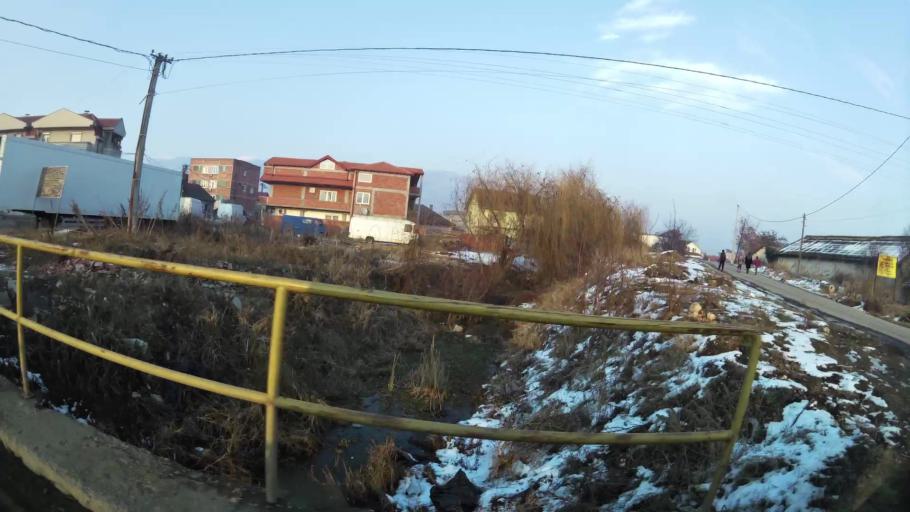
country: MK
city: Creshevo
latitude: 42.0161
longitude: 21.5125
